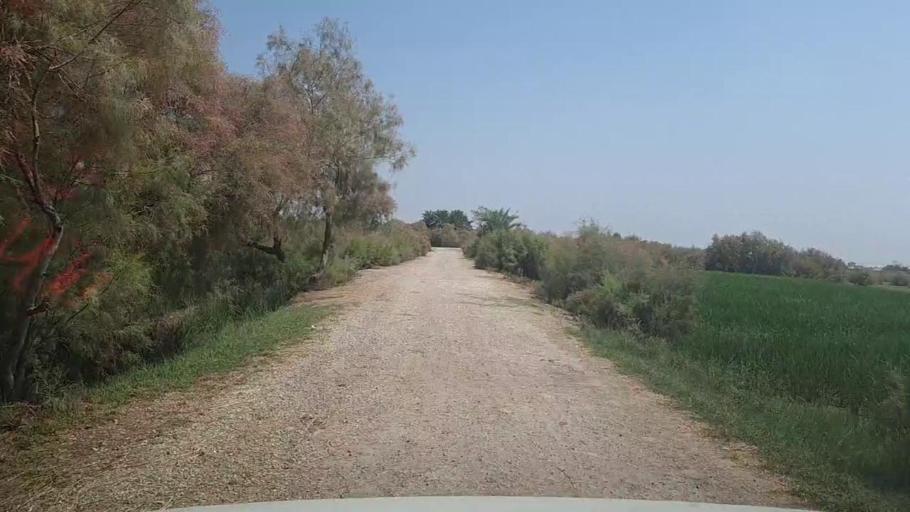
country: PK
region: Sindh
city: Kandhkot
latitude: 28.3062
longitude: 69.3571
